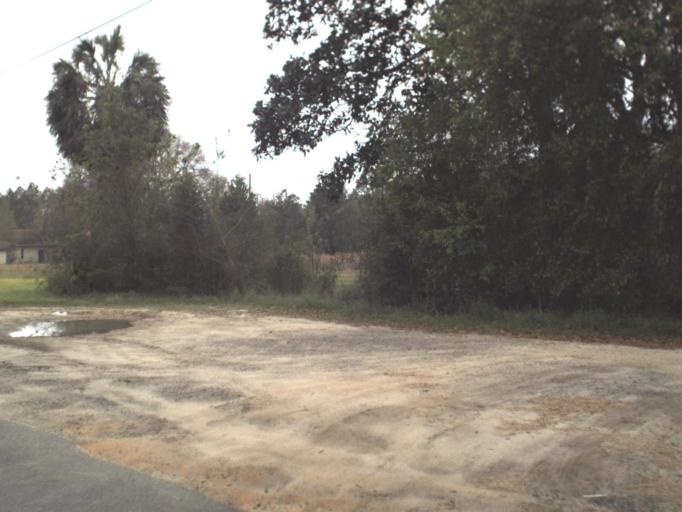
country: US
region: Florida
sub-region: Gulf County
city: Wewahitchka
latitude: 30.0917
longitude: -85.1957
